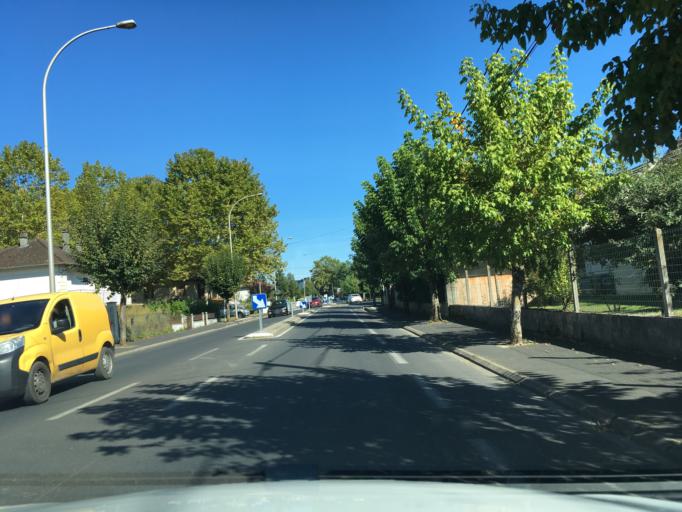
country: FR
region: Limousin
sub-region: Departement de la Correze
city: Ussac
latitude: 45.1568
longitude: 1.4893
